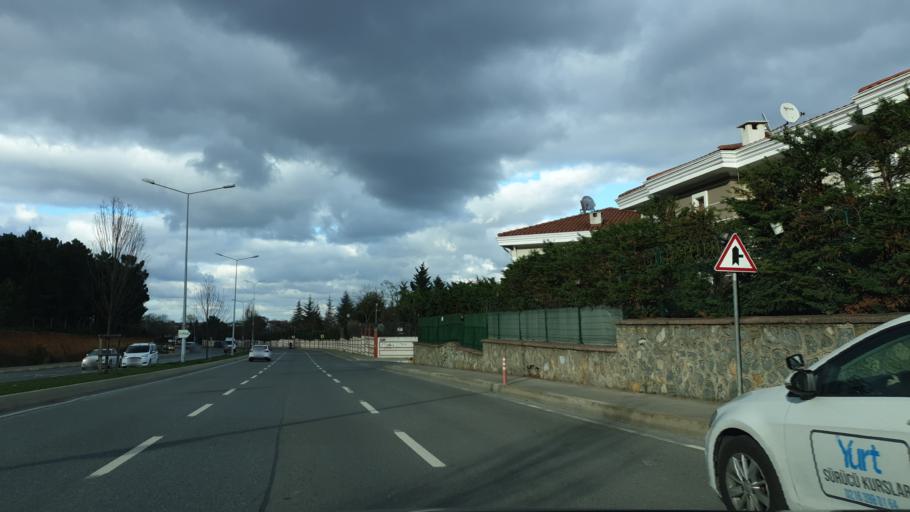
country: TR
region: Istanbul
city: Sultanbeyli
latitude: 40.9279
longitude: 29.2721
